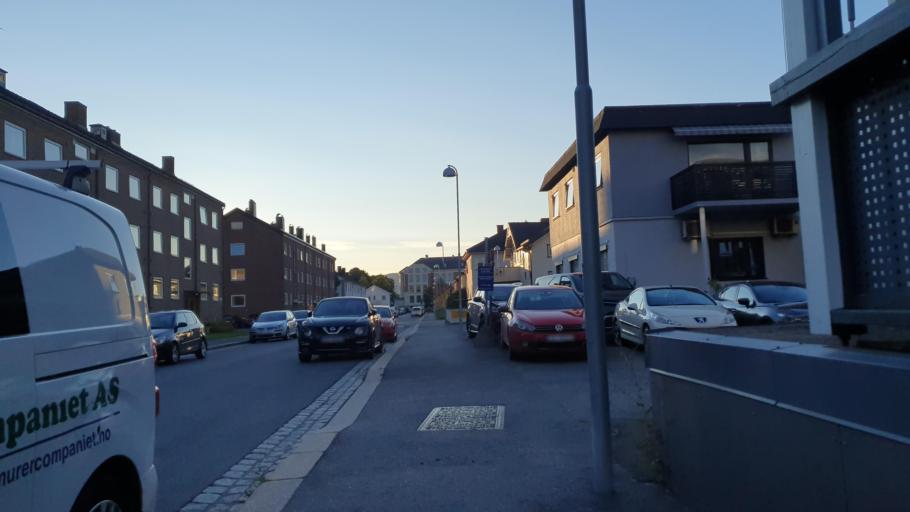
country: NO
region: Buskerud
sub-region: Drammen
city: Drammen
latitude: 59.7337
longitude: 10.2139
